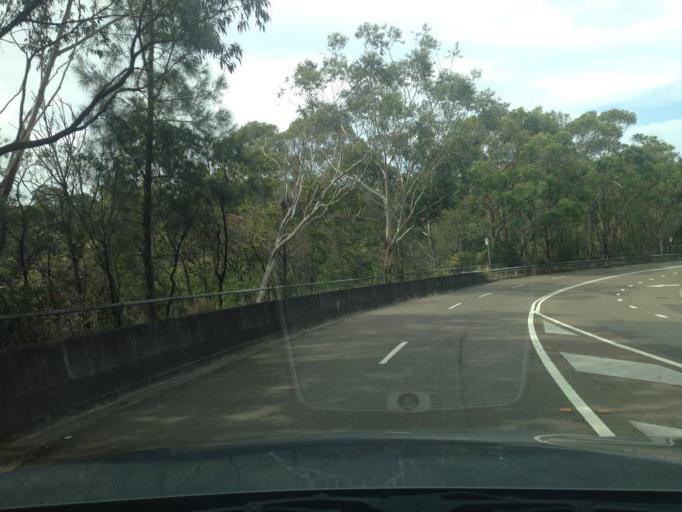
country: AU
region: New South Wales
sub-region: Lane Cove
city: Lane Cove West
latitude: -33.8074
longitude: 151.1491
